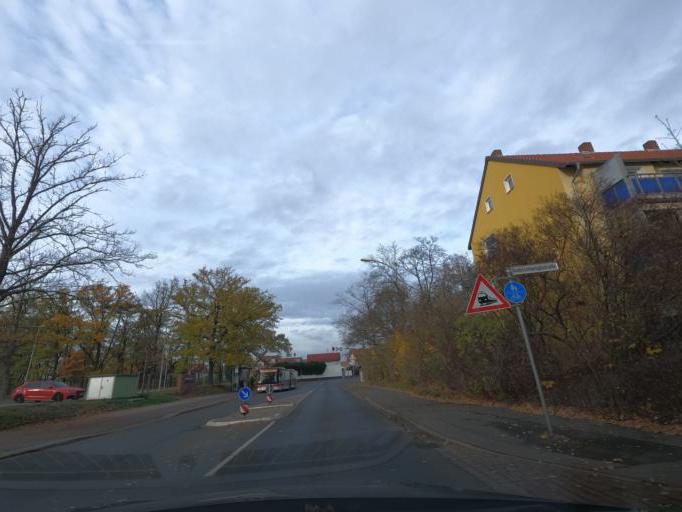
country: DE
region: Lower Saxony
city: Braunschweig
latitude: 52.3023
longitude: 10.5410
